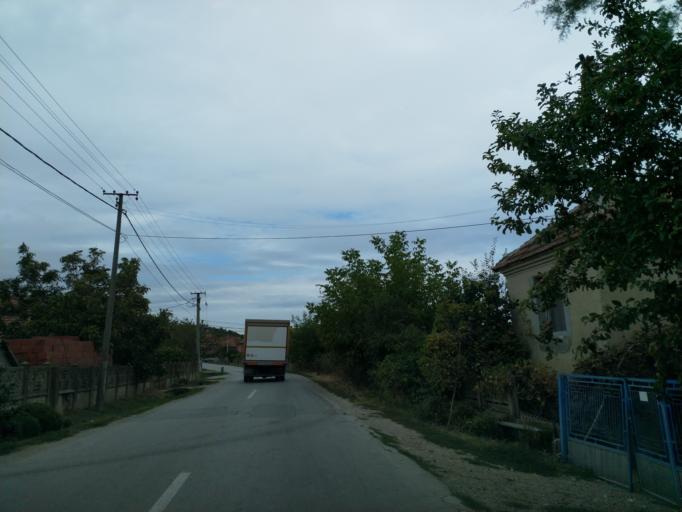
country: RS
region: Central Serbia
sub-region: Pomoravski Okrug
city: Cuprija
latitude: 43.8646
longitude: 21.3234
